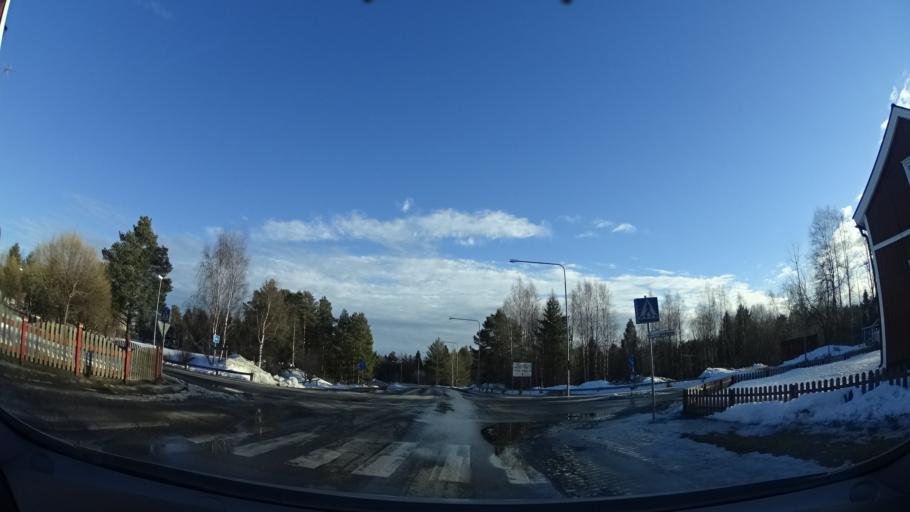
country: SE
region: Vaesterbotten
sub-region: Skelleftea Kommun
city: Byske
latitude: 64.9516
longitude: 21.2175
